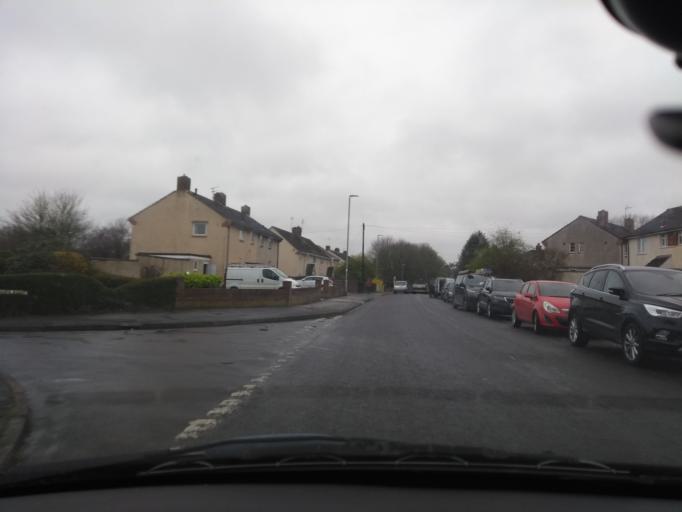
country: GB
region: England
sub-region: Somerset
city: Taunton
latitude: 51.0311
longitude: -3.1038
